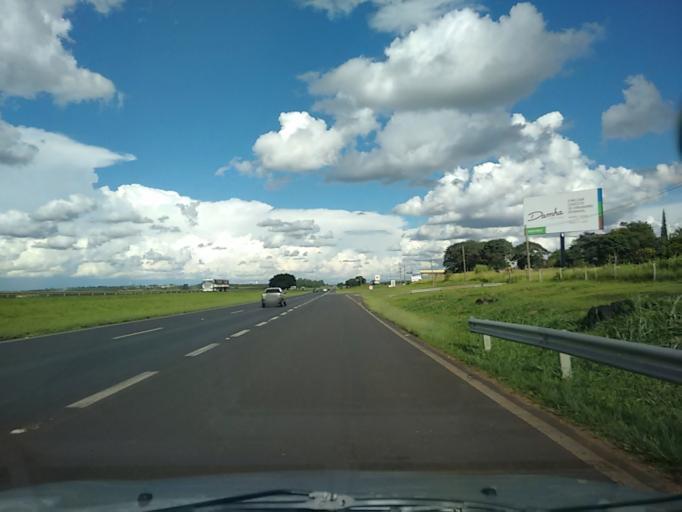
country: BR
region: Sao Paulo
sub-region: Ibate
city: Ibate
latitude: -21.9650
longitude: -47.9691
